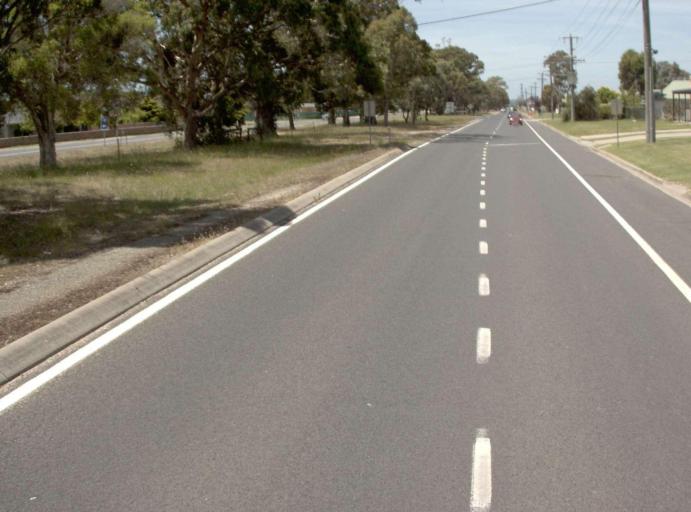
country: AU
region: Victoria
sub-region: East Gippsland
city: Bairnsdale
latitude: -37.8378
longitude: 147.5976
